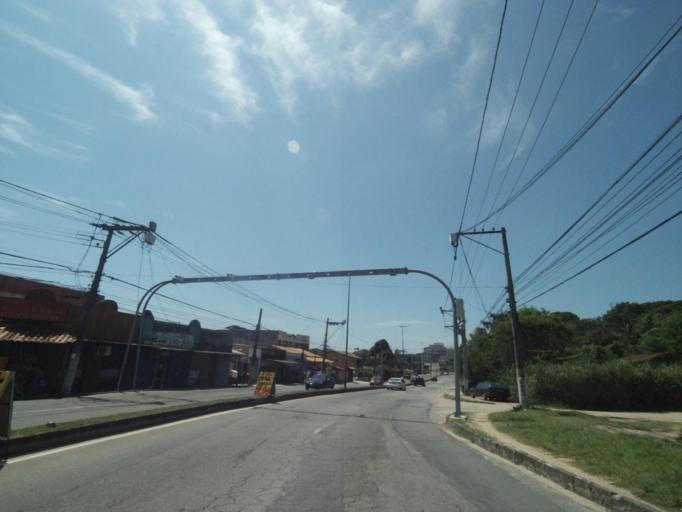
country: BR
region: Rio de Janeiro
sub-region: Sao Goncalo
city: Sao Goncalo
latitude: -22.8876
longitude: -43.0332
